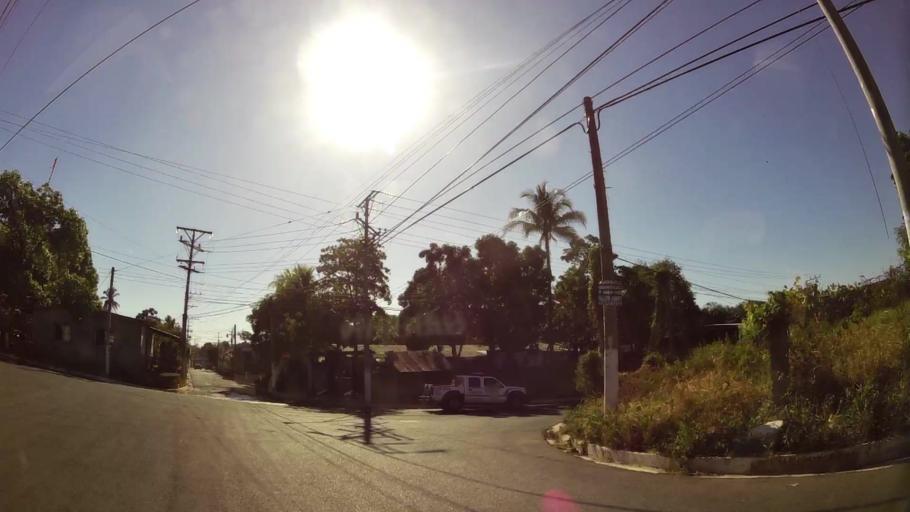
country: SV
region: Sonsonate
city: Sonzacate
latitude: 13.7377
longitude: -89.7167
